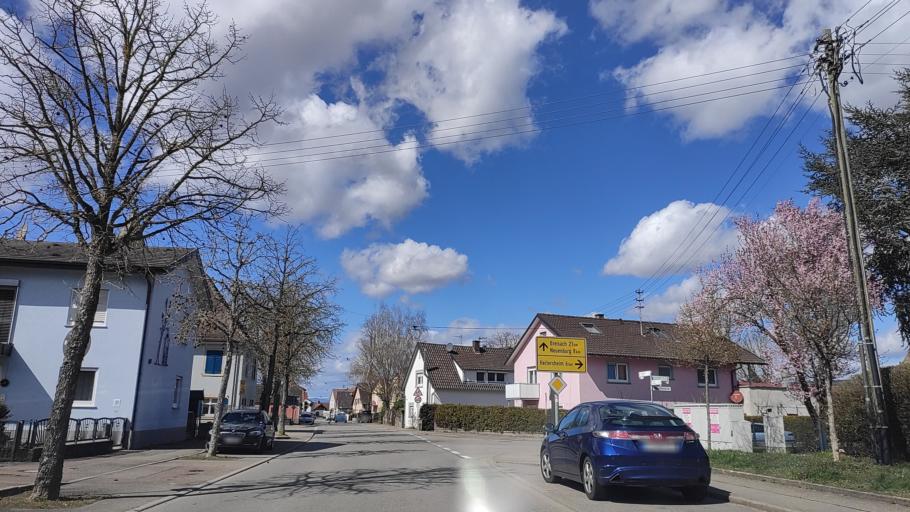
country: DE
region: Baden-Wuerttemberg
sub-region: Freiburg Region
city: Buggingen
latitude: 47.8727
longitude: 7.5935
